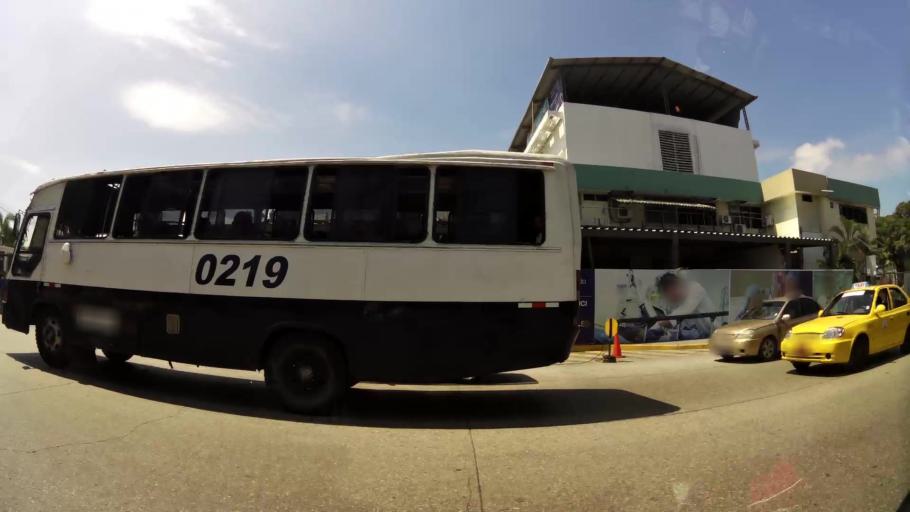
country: EC
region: Guayas
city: Guayaquil
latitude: -2.2323
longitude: -79.8996
